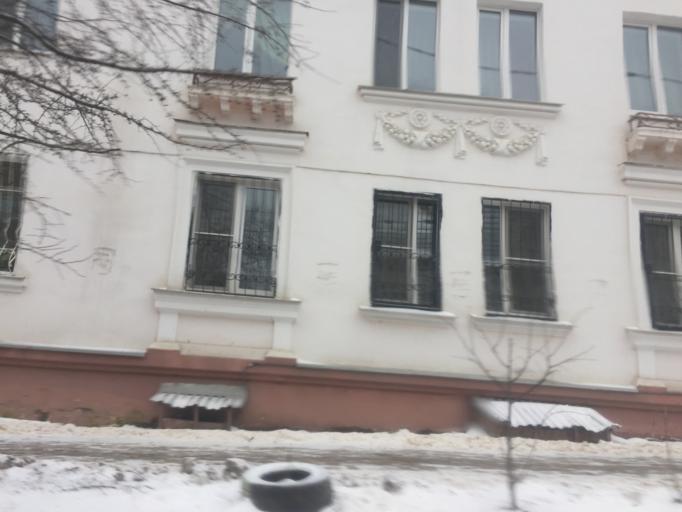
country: RU
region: Tula
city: Mendeleyevskiy
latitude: 54.1681
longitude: 37.5981
